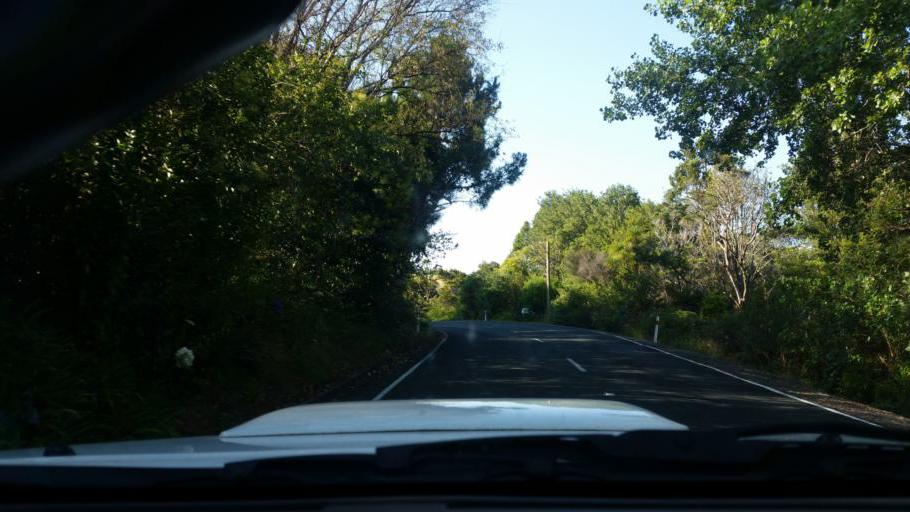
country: NZ
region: Northland
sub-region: Whangarei
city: Ruakaka
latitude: -36.1091
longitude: 174.2293
